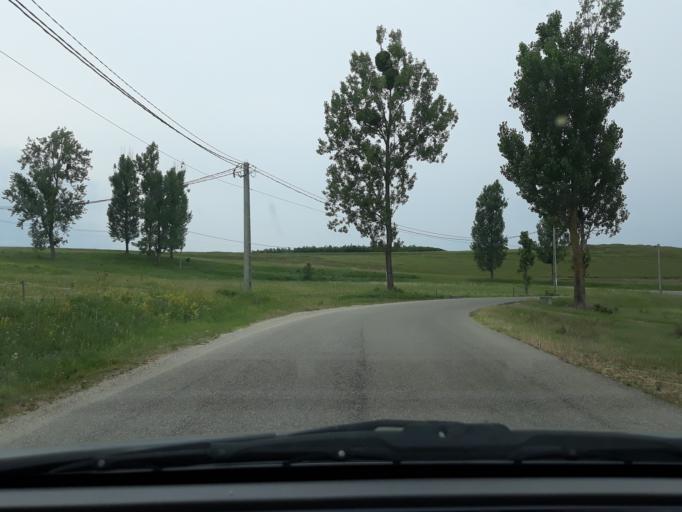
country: RO
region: Salaj
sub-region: Comuna Criseni
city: Criseni
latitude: 47.2448
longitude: 23.0694
